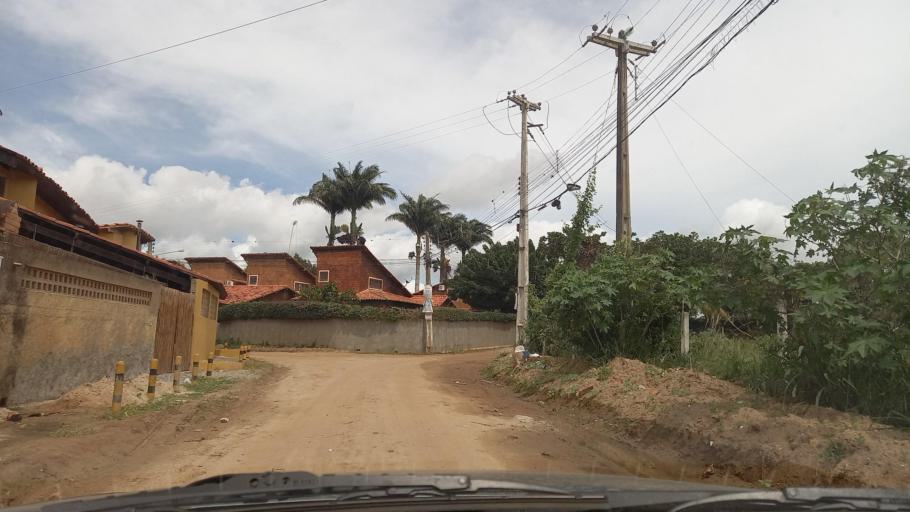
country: BR
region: Pernambuco
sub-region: Gravata
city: Gravata
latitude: -8.1954
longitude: -35.5892
